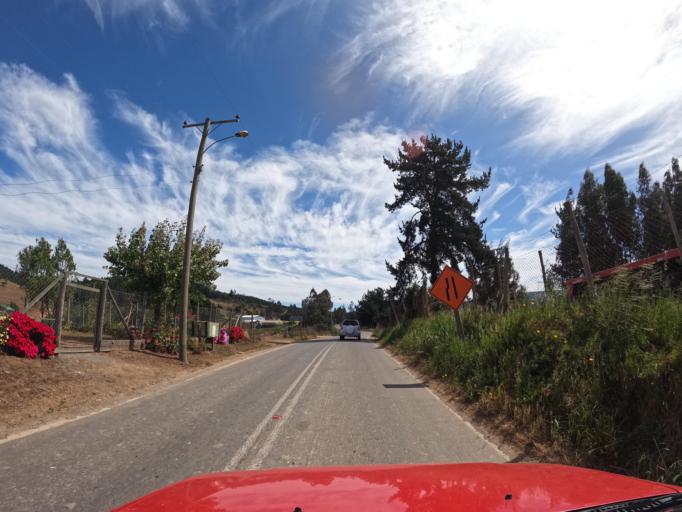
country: CL
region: Maule
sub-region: Provincia de Talca
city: Constitucion
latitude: -34.9921
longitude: -72.0047
